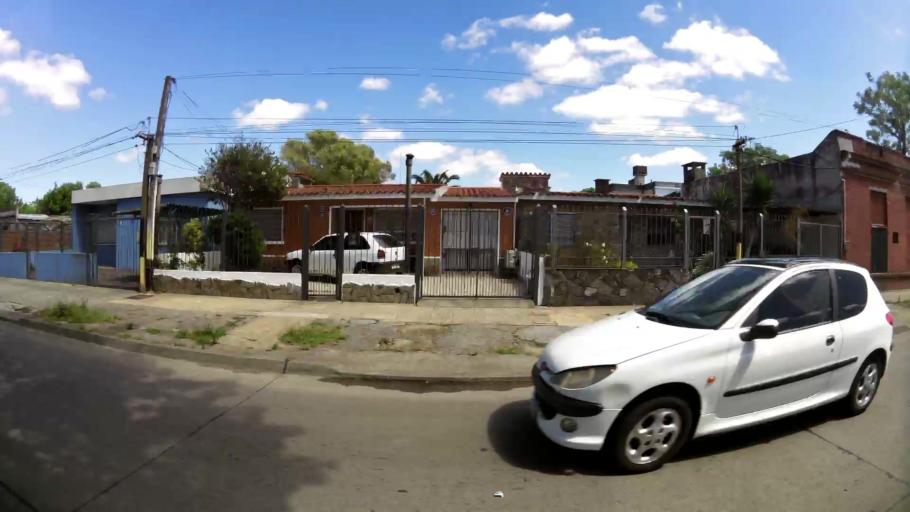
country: UY
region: Montevideo
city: Montevideo
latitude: -34.8506
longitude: -56.1359
